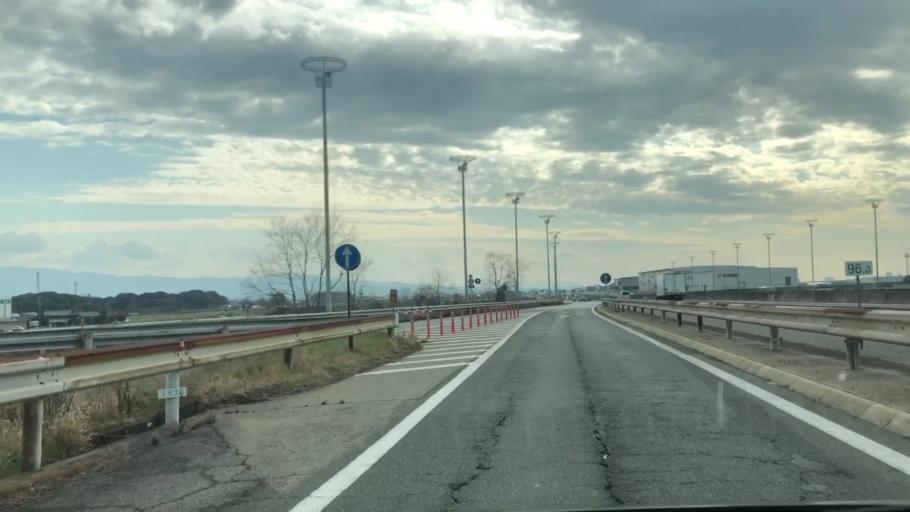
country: JP
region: Saga Prefecture
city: Tosu
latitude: 33.3950
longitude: 130.5386
